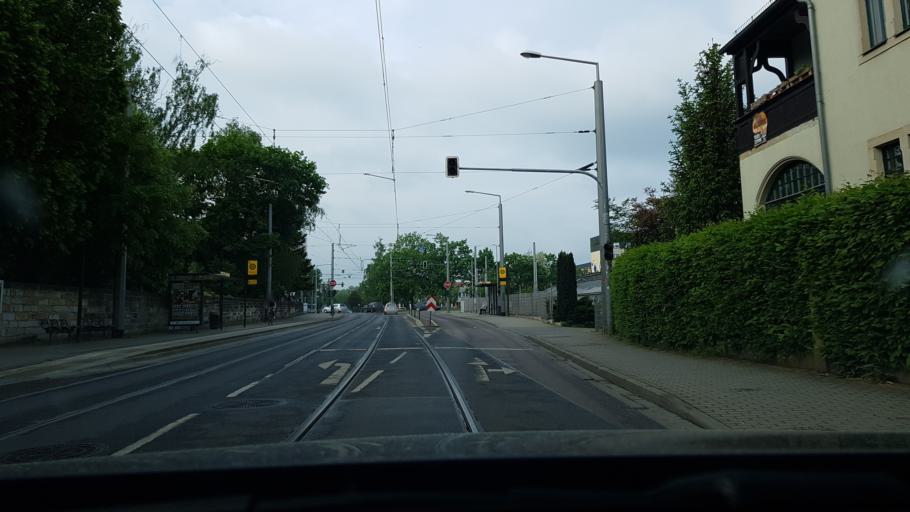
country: DE
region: Saxony
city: Heidenau
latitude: 51.0138
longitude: 13.8246
